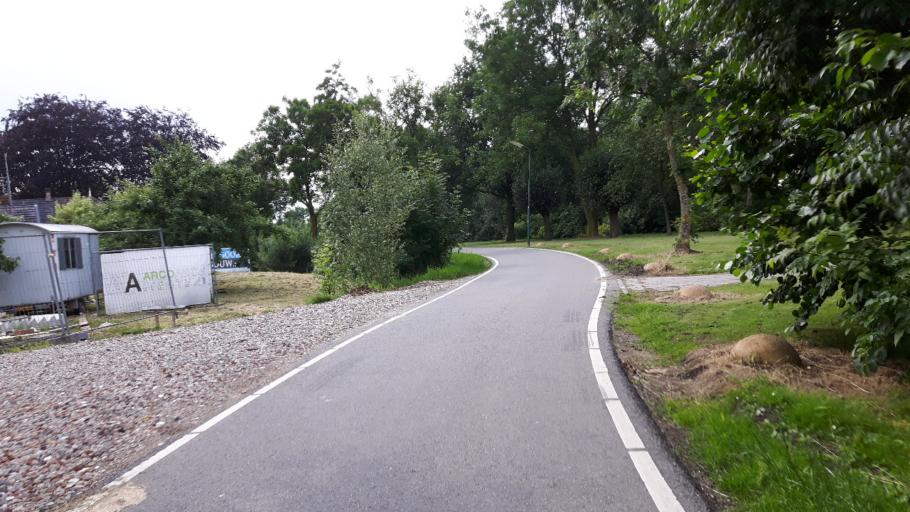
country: NL
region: Utrecht
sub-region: Gemeente Woerden
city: Woerden
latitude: 52.1048
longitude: 4.9315
